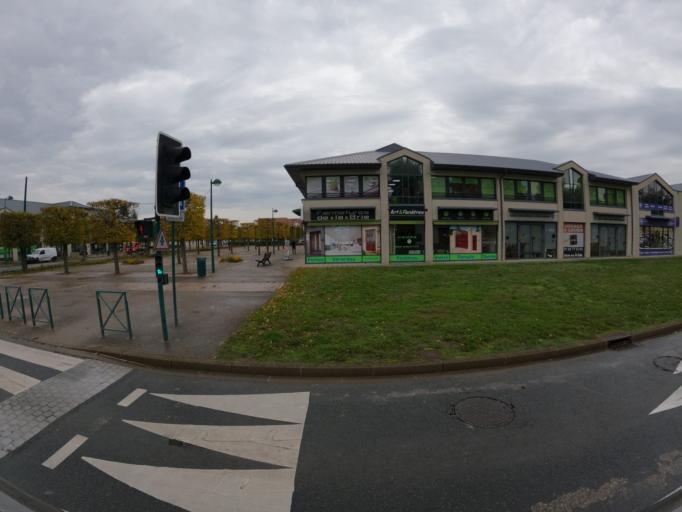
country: FR
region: Ile-de-France
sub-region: Departement de Seine-et-Marne
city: Serris
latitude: 48.8412
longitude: 2.7910
